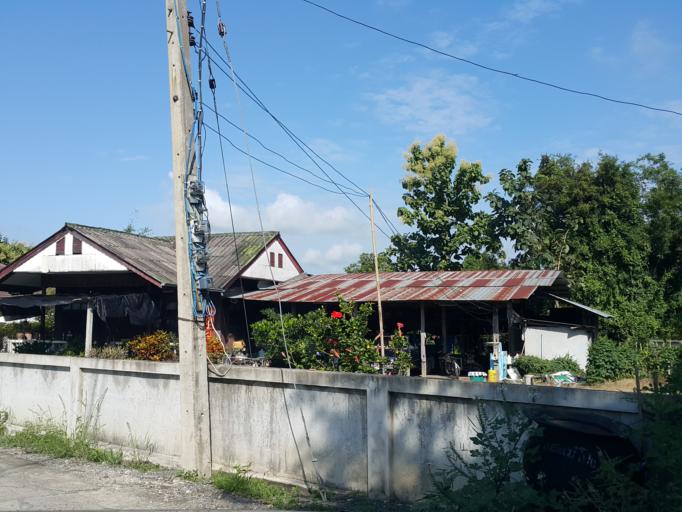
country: TH
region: Chiang Mai
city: San Kamphaeng
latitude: 18.8216
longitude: 99.1676
